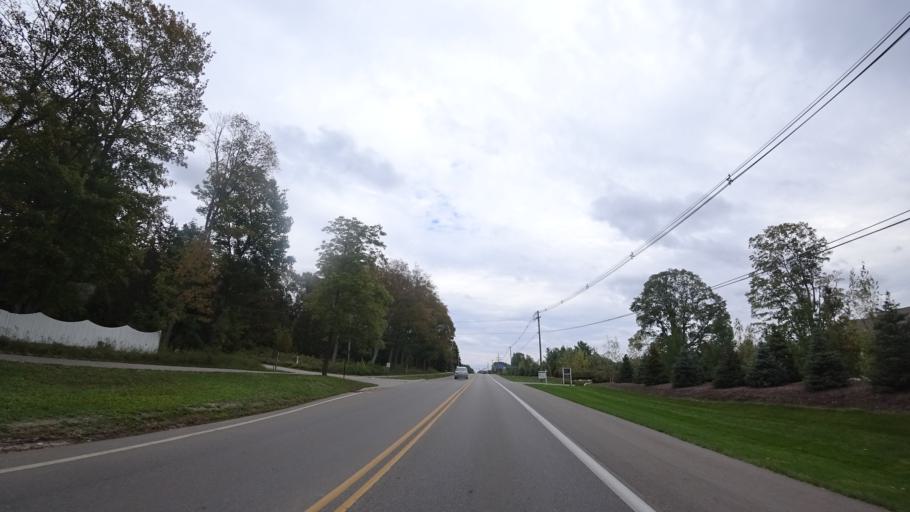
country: US
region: Michigan
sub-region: Emmet County
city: Petoskey
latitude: 45.4281
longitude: -84.9169
